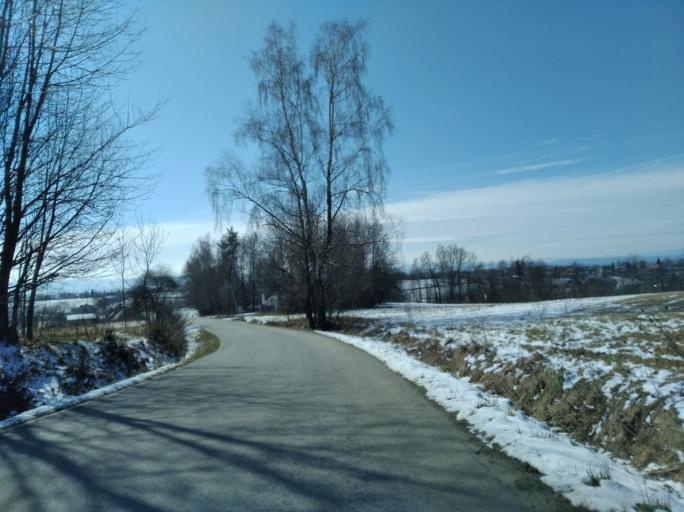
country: PL
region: Subcarpathian Voivodeship
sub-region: Powiat brzozowski
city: Jablonica Polska
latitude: 49.7190
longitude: 21.8817
